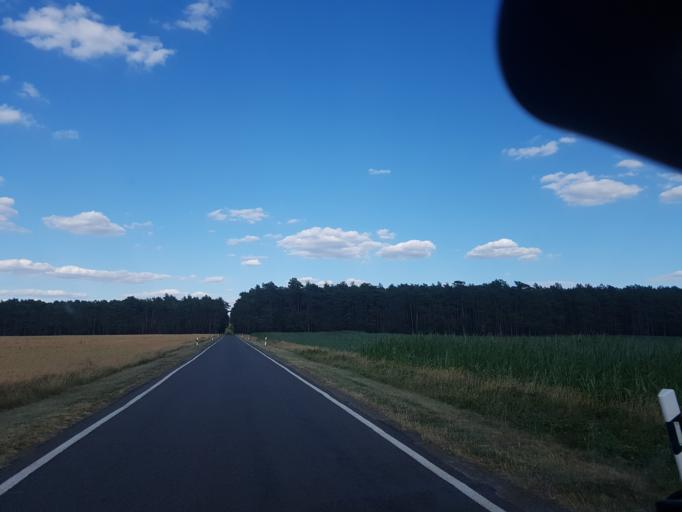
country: DE
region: Brandenburg
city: Herzberg
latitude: 51.7831
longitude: 13.2455
